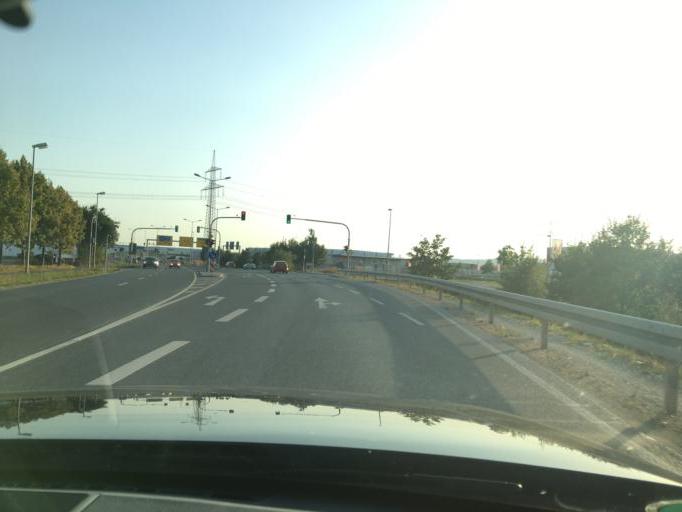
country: DE
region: Bavaria
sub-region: Upper Franconia
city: Forchheim
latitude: 49.7013
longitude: 11.0604
